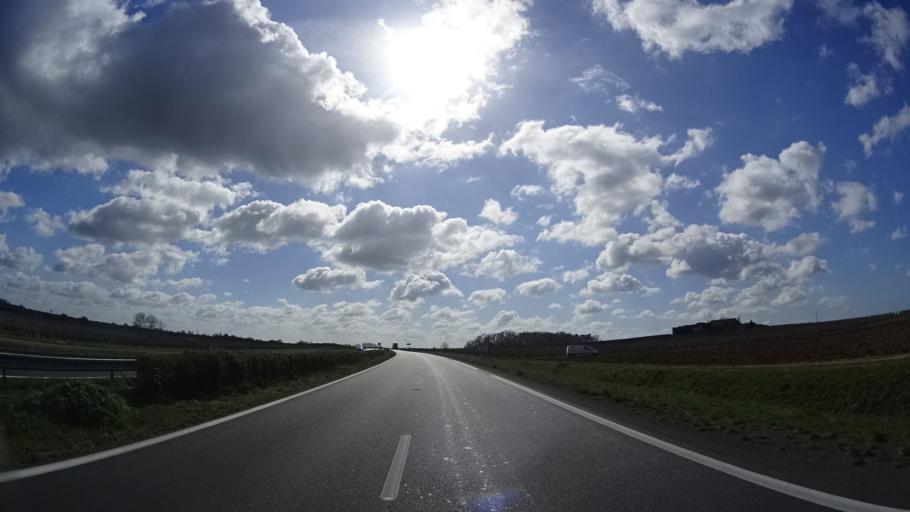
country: FR
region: Pays de la Loire
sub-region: Departement de Maine-et-Loire
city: Saint-Melaine-sur-Aubance
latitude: 47.3777
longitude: -0.4727
